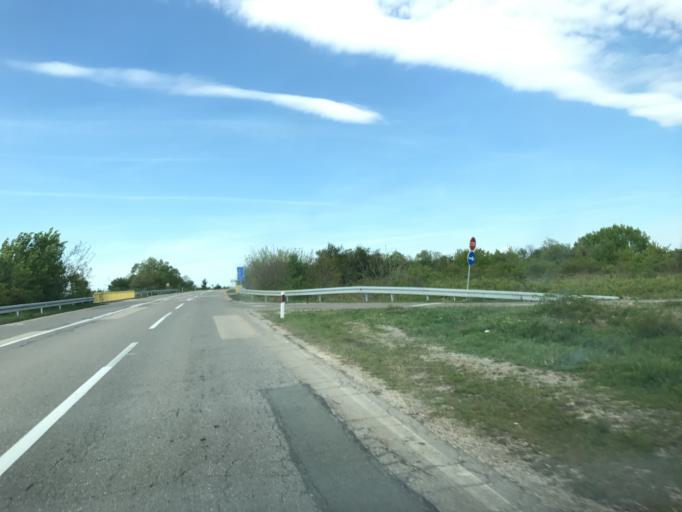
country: RS
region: Central Serbia
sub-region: Borski Okrug
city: Negotin
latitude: 44.1227
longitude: 22.3407
